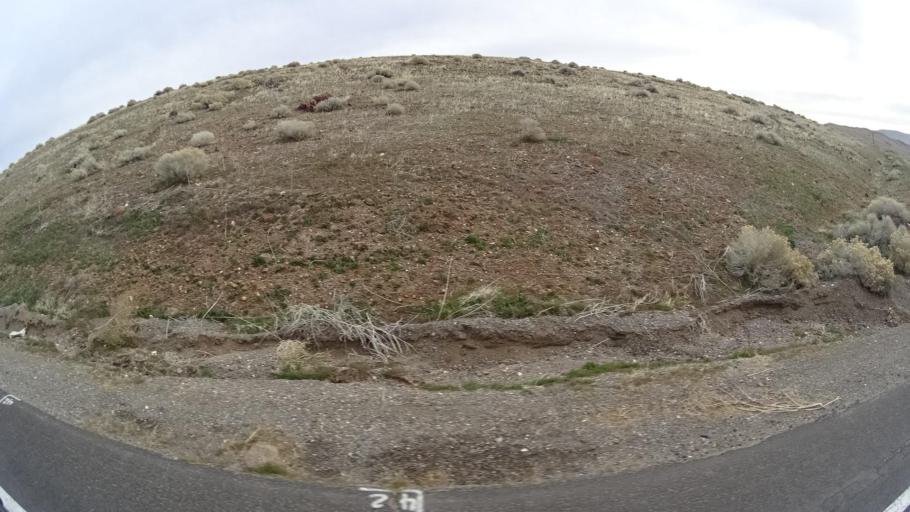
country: US
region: Nevada
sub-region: Washoe County
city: Sun Valley
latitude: 39.5718
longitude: -119.7877
